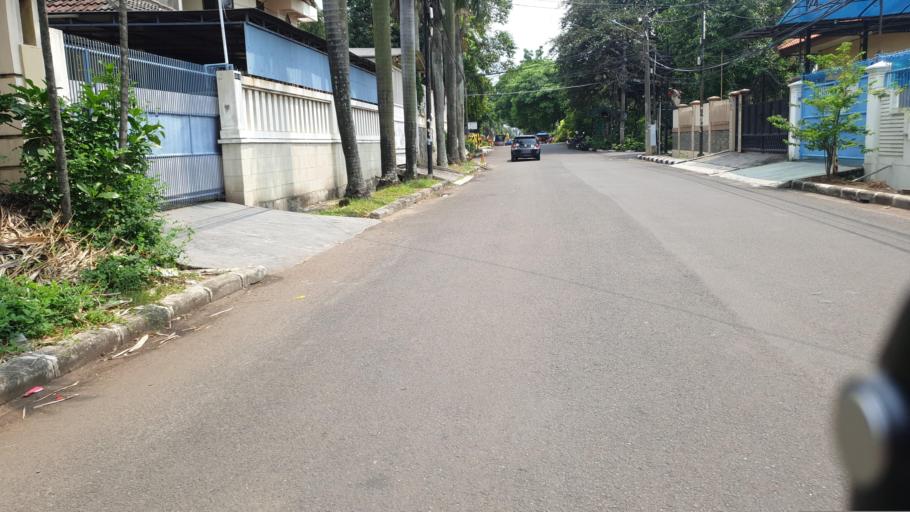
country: ID
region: West Java
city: Ciputat
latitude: -6.1953
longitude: 106.7471
